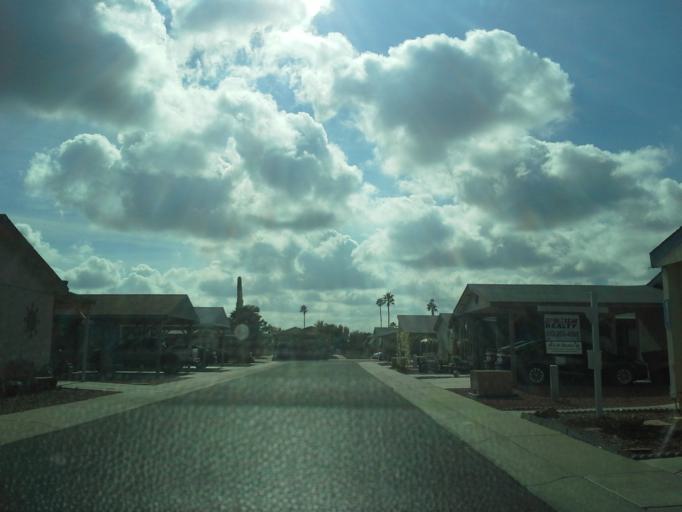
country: US
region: Arizona
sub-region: Maricopa County
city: Sun City
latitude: 33.5854
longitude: -112.2687
